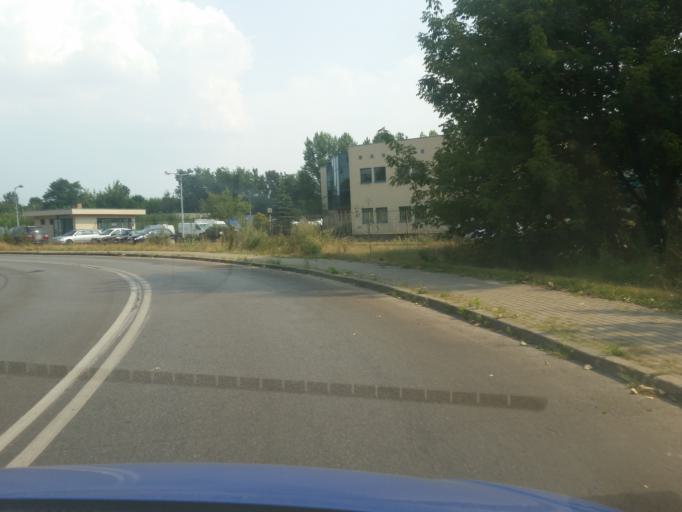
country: PL
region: Silesian Voivodeship
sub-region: Sosnowiec
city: Sosnowiec
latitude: 50.2641
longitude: 19.1338
